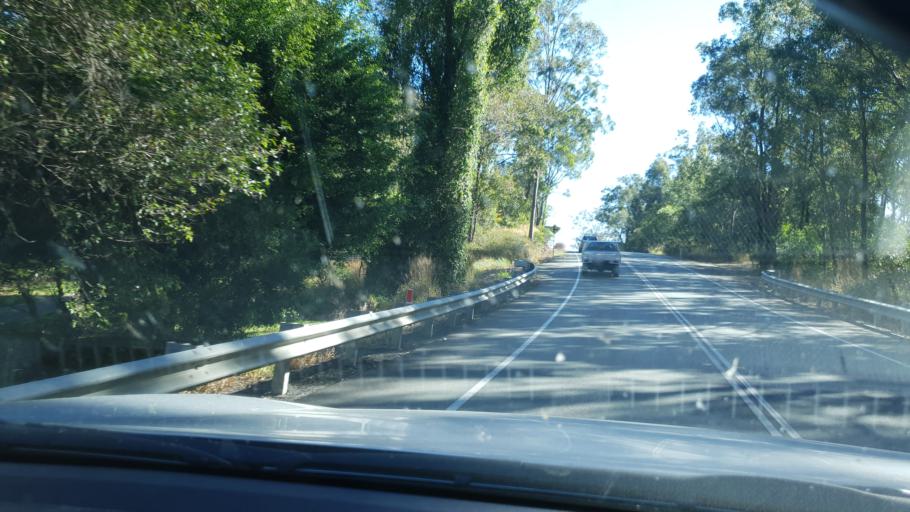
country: AU
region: Queensland
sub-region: Moreton Bay
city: Strathpine
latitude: -27.3292
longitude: 152.9470
